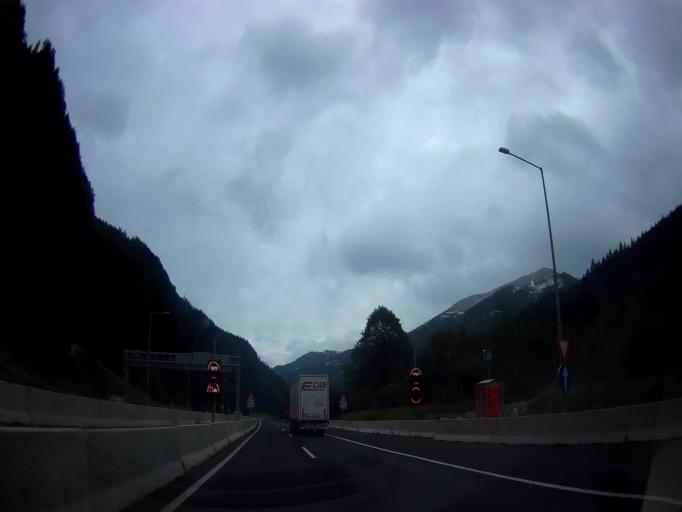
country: AT
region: Styria
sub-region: Politischer Bezirk Leoben
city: Wald am Schoberpass
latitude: 47.4413
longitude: 14.6891
